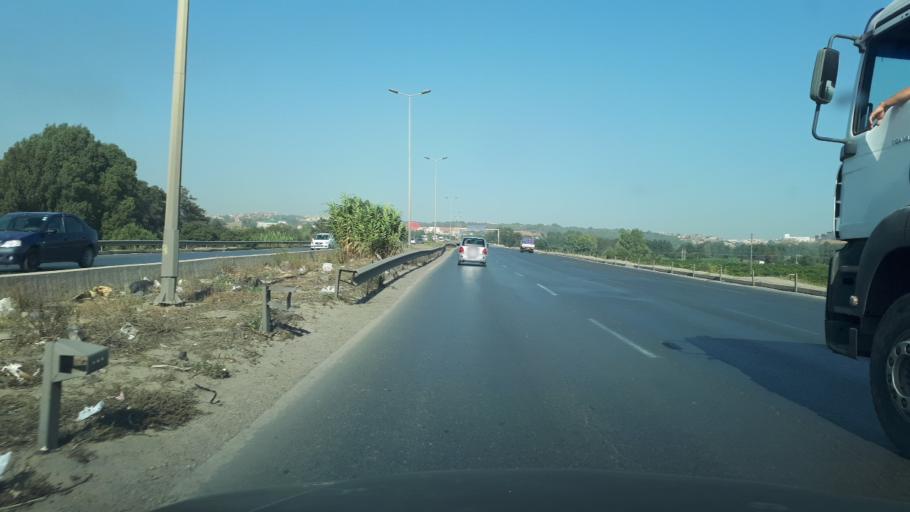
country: DZ
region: Tipaza
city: Baraki
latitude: 36.6768
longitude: 3.0709
